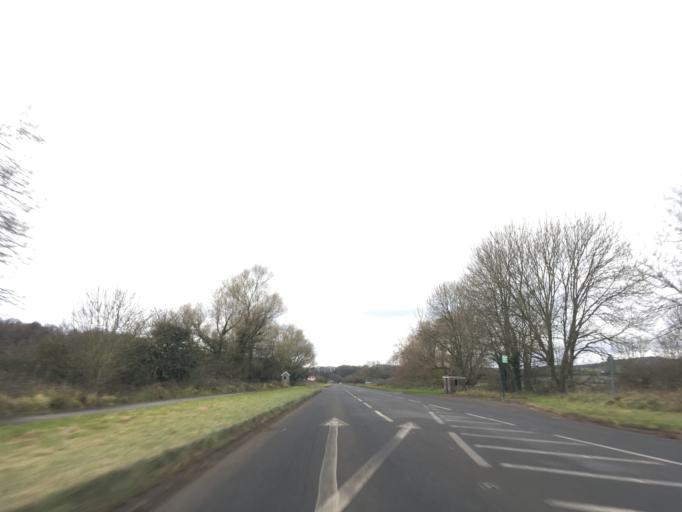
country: GB
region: Wales
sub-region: Monmouthshire
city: Rogiet
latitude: 51.6127
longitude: -2.7840
